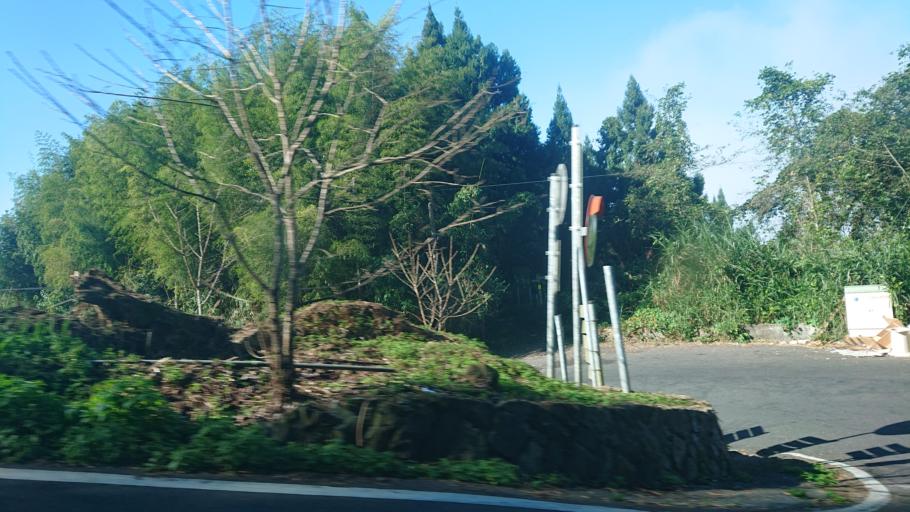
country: TW
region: Taiwan
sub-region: Chiayi
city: Jiayi Shi
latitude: 23.4802
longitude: 120.6986
